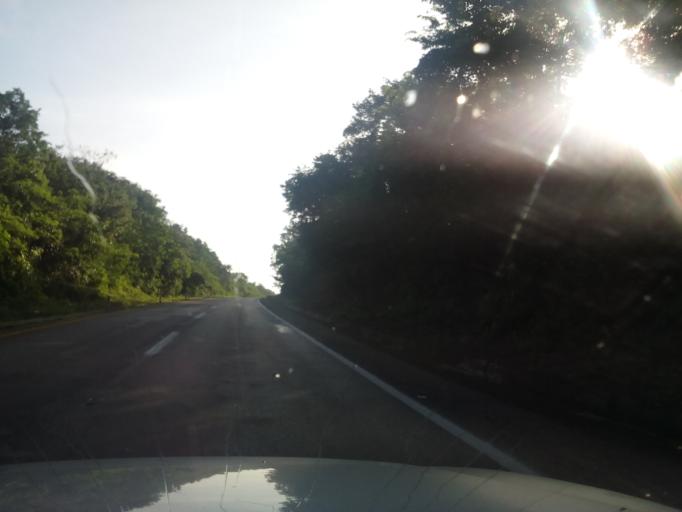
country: MX
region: Yucatan
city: Tinum
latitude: 20.7156
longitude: -88.4161
